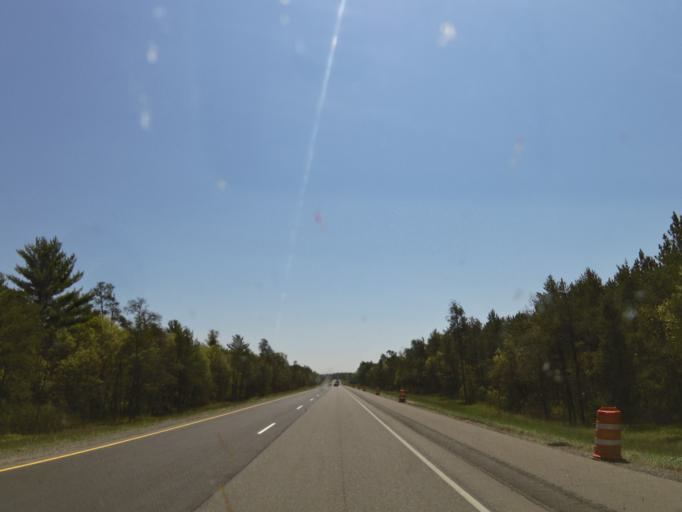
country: US
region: Wisconsin
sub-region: Jackson County
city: Black River Falls
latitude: 44.2071
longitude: -90.6653
